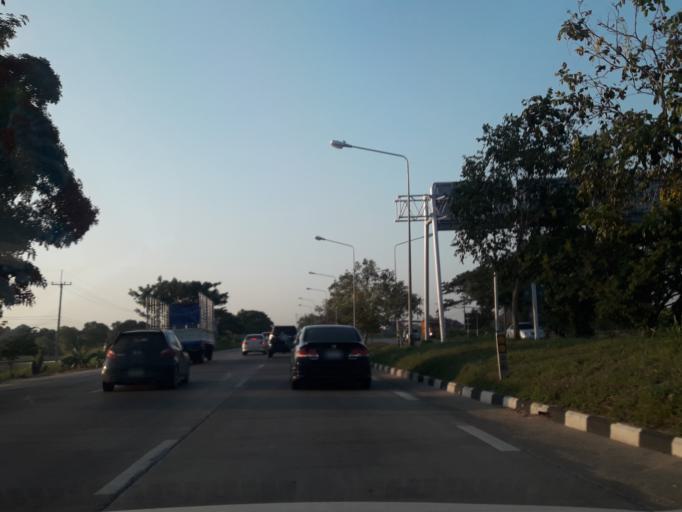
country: TH
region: Phra Nakhon Si Ayutthaya
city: Phra Nakhon Si Ayutthaya
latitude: 14.3498
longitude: 100.5284
